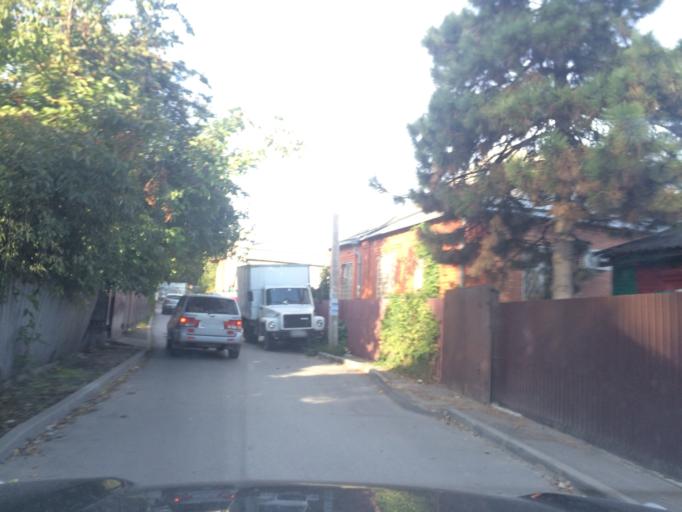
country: RU
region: Rostov
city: Rostov-na-Donu
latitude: 47.2116
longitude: 39.6912
